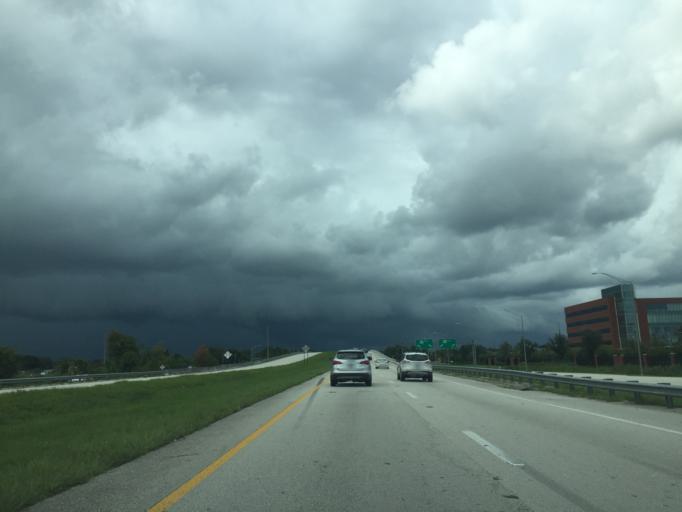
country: US
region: Florida
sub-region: Orange County
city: Lockhart
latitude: 28.6407
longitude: -81.4111
